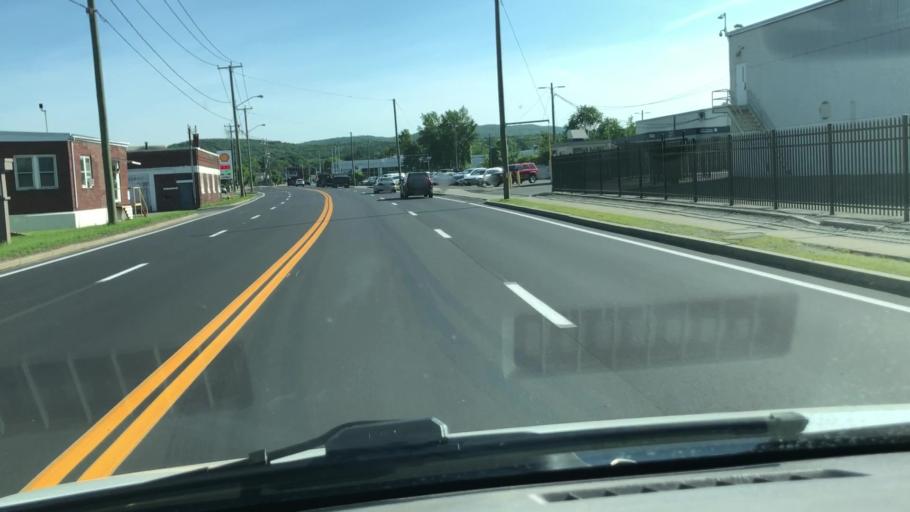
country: US
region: Massachusetts
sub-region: Berkshire County
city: Pittsfield
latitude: 42.4623
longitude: -73.2070
